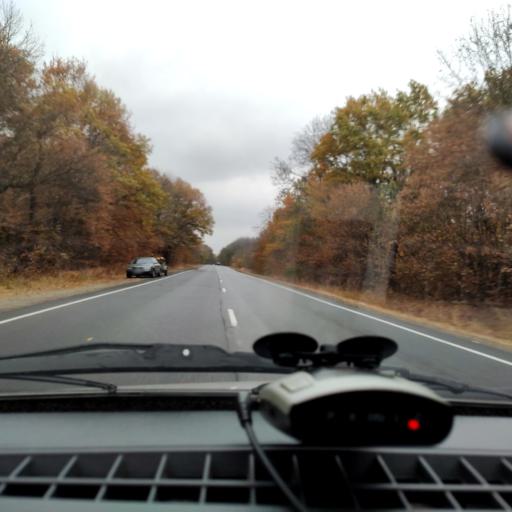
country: RU
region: Voronezj
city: Devitsa
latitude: 51.6266
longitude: 38.9894
